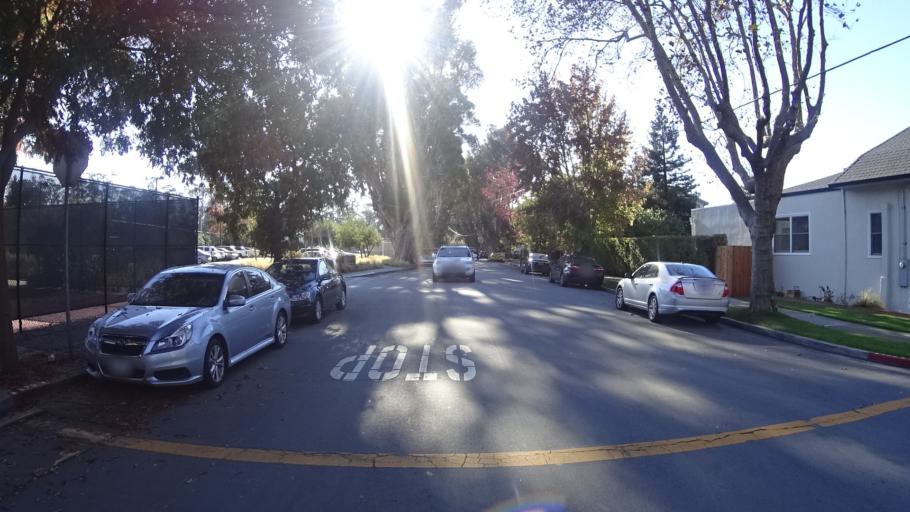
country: US
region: California
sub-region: San Mateo County
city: Burlingame
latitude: 37.5845
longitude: -122.3479
